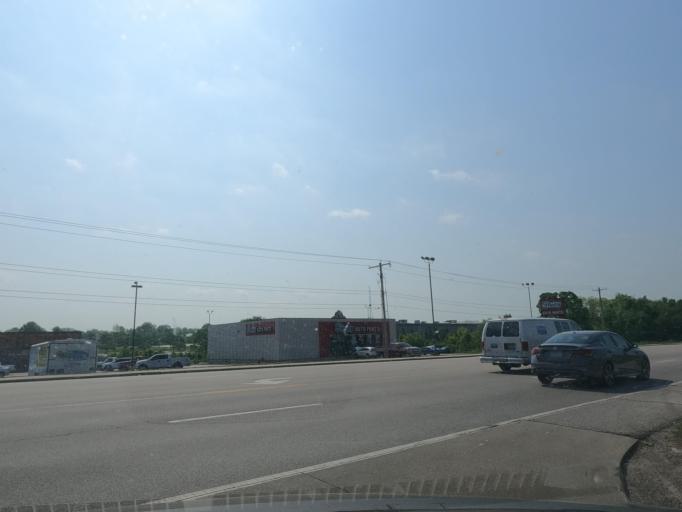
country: US
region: Missouri
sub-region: Greene County
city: Springfield
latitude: 37.1432
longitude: -93.2962
